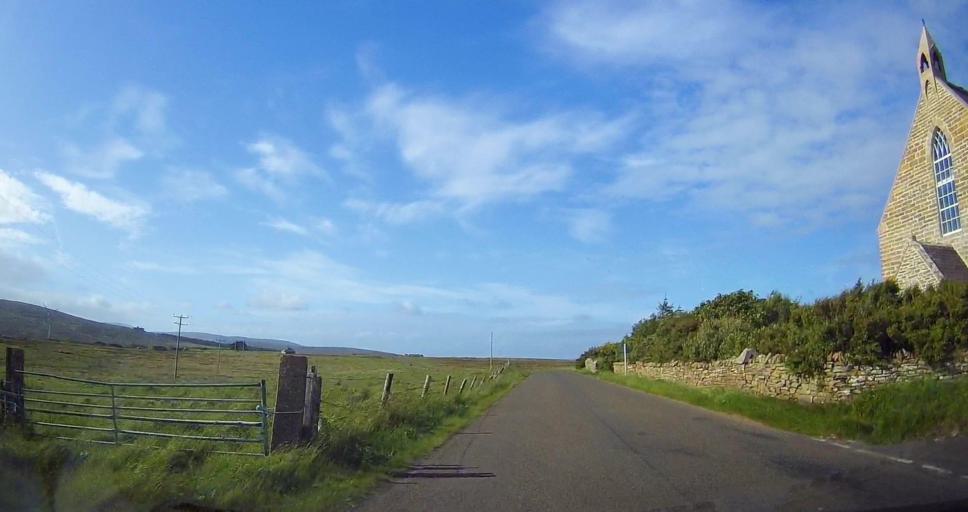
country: GB
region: Scotland
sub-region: Orkney Islands
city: Stromness
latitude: 58.8175
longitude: -3.2027
